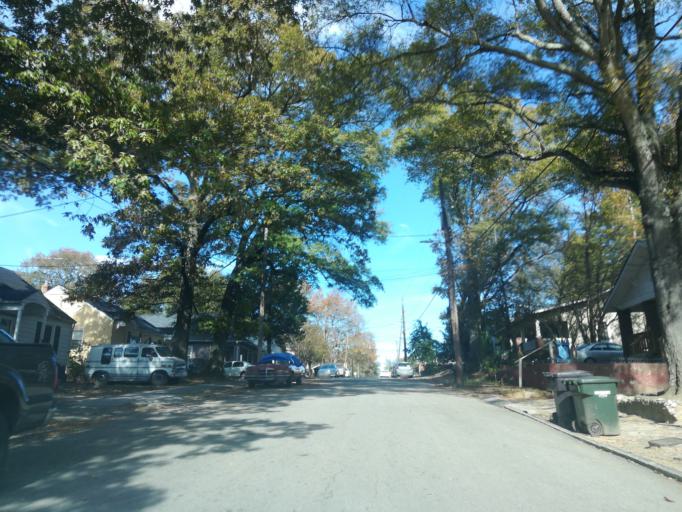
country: US
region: North Carolina
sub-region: Durham County
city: Durham
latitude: 35.9875
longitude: -78.8805
